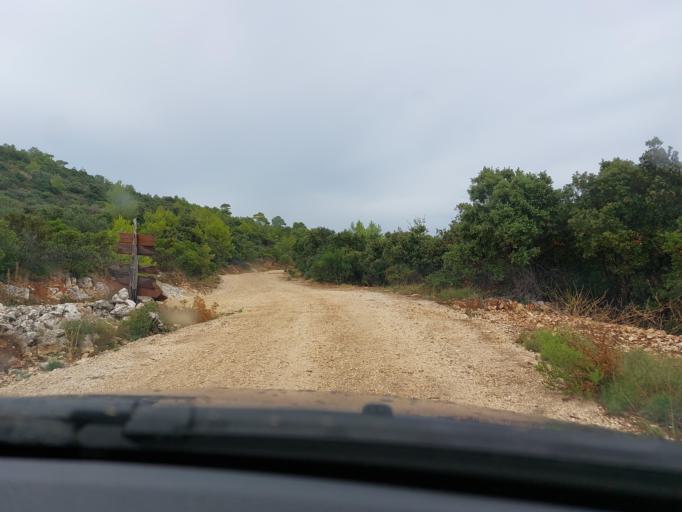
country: HR
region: Dubrovacko-Neretvanska
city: Smokvica
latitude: 42.7426
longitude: 16.9130
